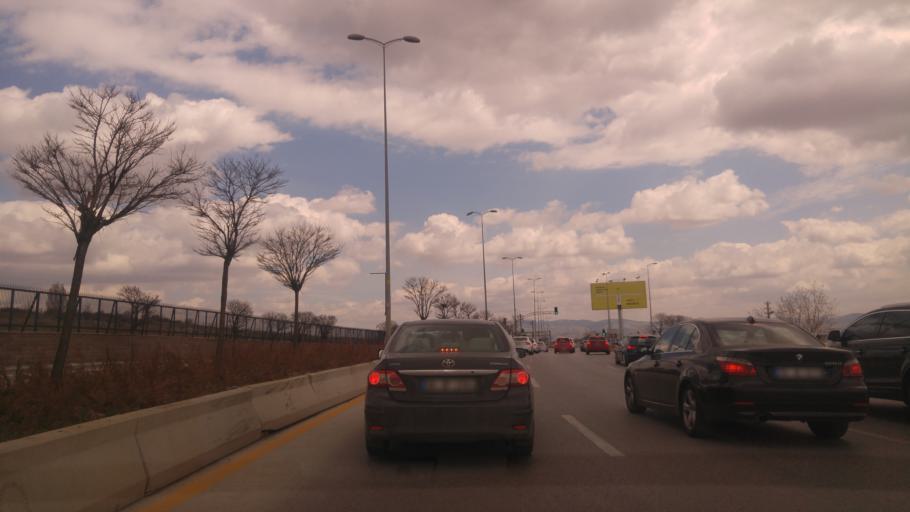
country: TR
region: Ankara
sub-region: Goelbasi
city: Golbasi
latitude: 39.8364
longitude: 32.7635
